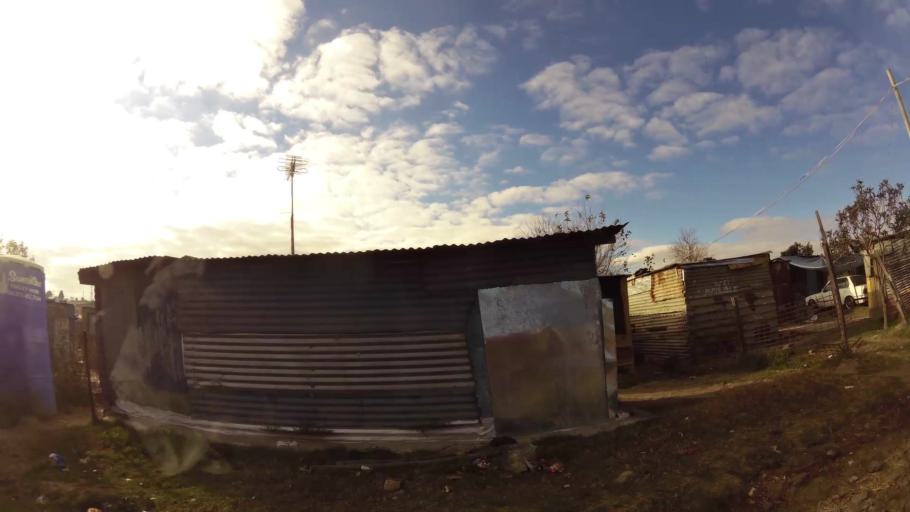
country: ZA
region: Gauteng
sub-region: Ekurhuleni Metropolitan Municipality
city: Tembisa
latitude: -26.0358
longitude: 28.1889
